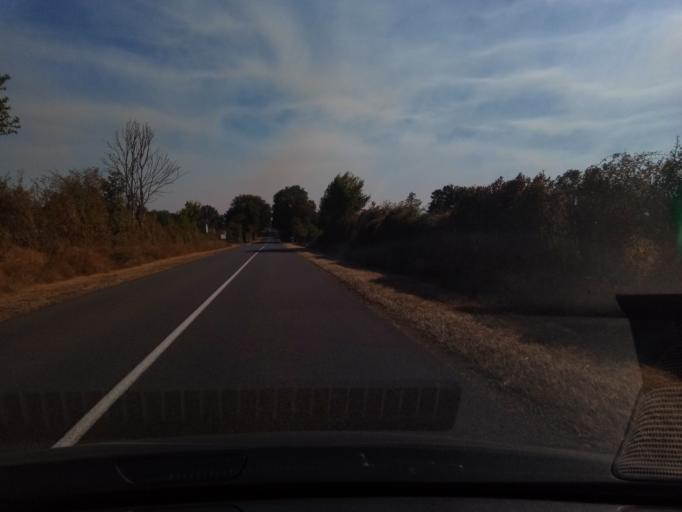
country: FR
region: Poitou-Charentes
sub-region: Departement de la Vienne
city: Montmorillon
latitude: 46.4879
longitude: 0.7866
